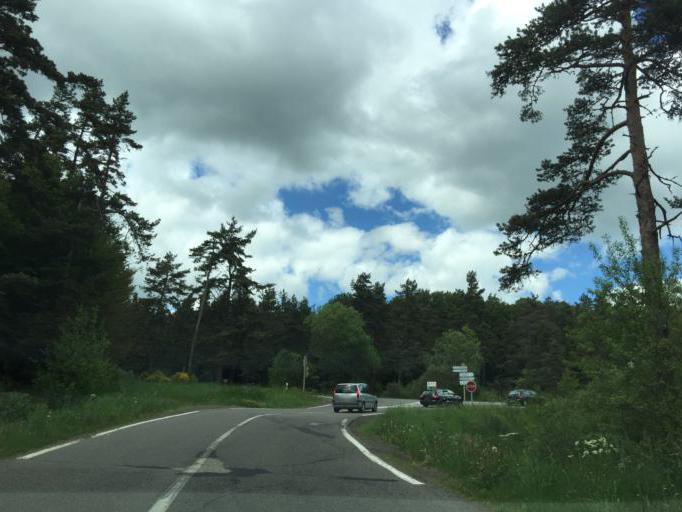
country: FR
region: Rhone-Alpes
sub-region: Departement de la Loire
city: Montbrison
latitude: 45.5447
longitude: 3.9544
